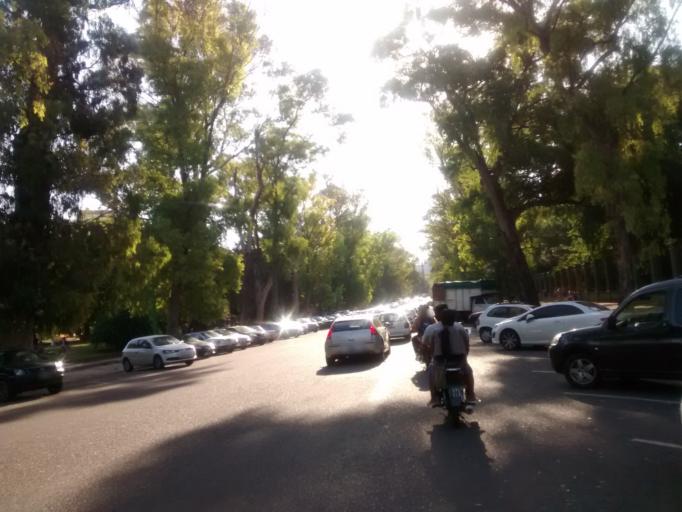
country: AR
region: Buenos Aires
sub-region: Partido de La Plata
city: La Plata
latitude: -34.9097
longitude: -57.9378
